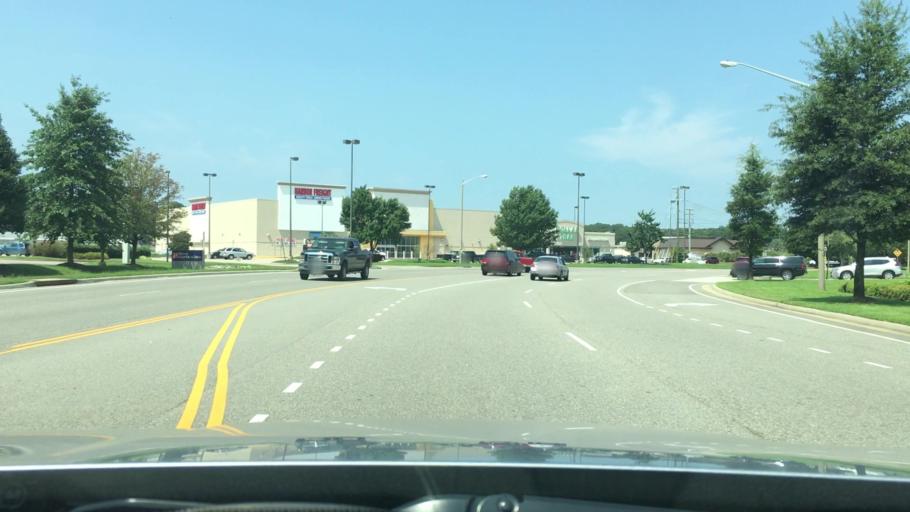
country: US
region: Virginia
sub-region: City of Colonial Heights
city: Colonial Heights
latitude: 37.2499
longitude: -77.3907
